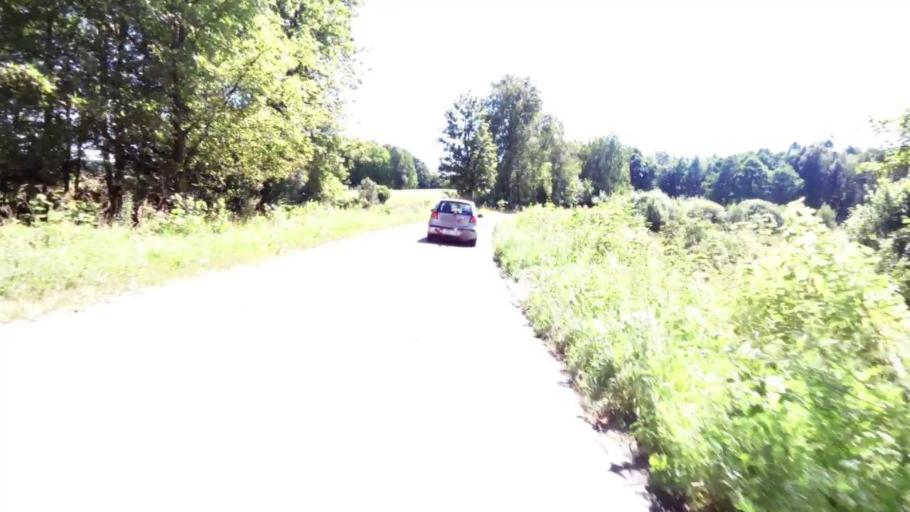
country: PL
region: West Pomeranian Voivodeship
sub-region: Powiat szczecinecki
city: Bialy Bor
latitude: 53.9664
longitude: 16.8652
